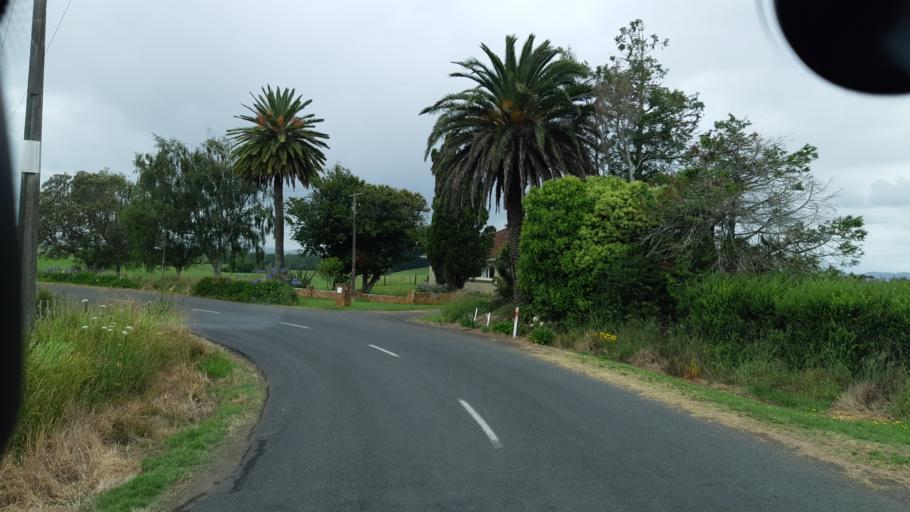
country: NZ
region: Waikato
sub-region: Waikato District
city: Te Kauwhata
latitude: -37.5133
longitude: 175.0846
